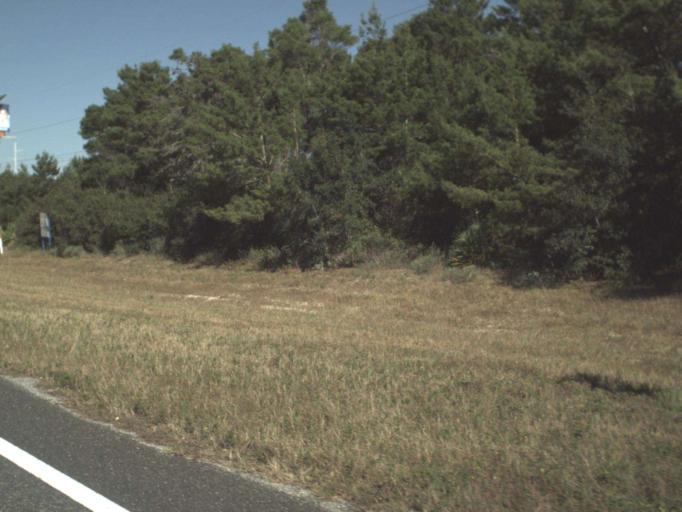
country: US
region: Florida
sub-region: Bay County
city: Laguna Beach
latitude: 30.2500
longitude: -85.9319
